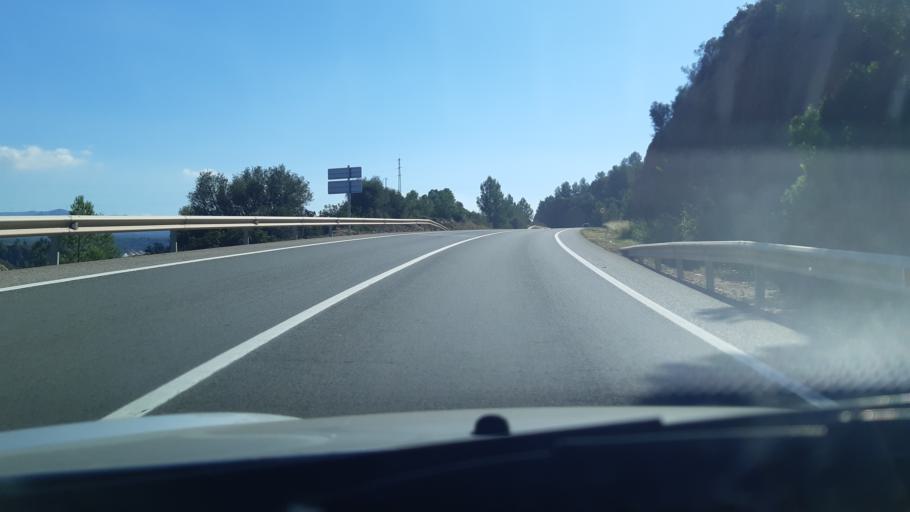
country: ES
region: Catalonia
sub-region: Provincia de Tarragona
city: Tivenys
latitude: 40.9281
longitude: 0.4862
